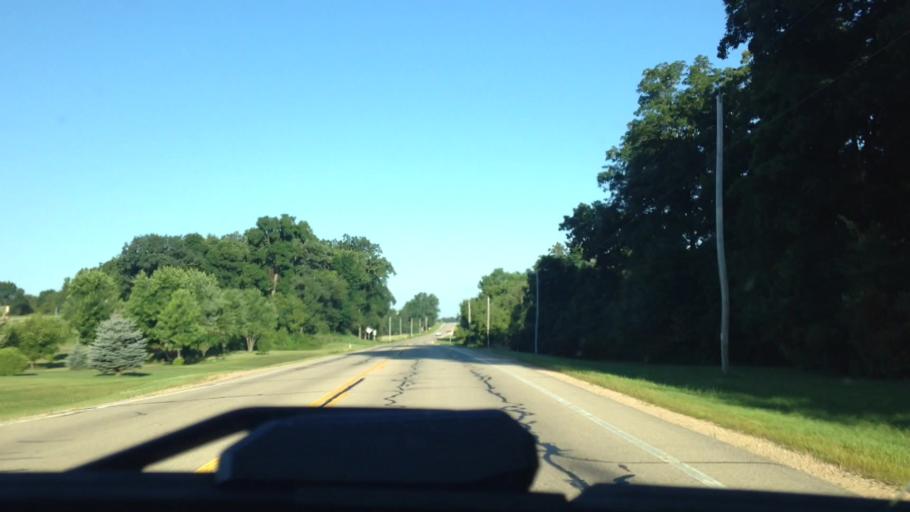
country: US
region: Wisconsin
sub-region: Columbia County
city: Fall River
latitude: 43.3406
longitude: -89.1477
